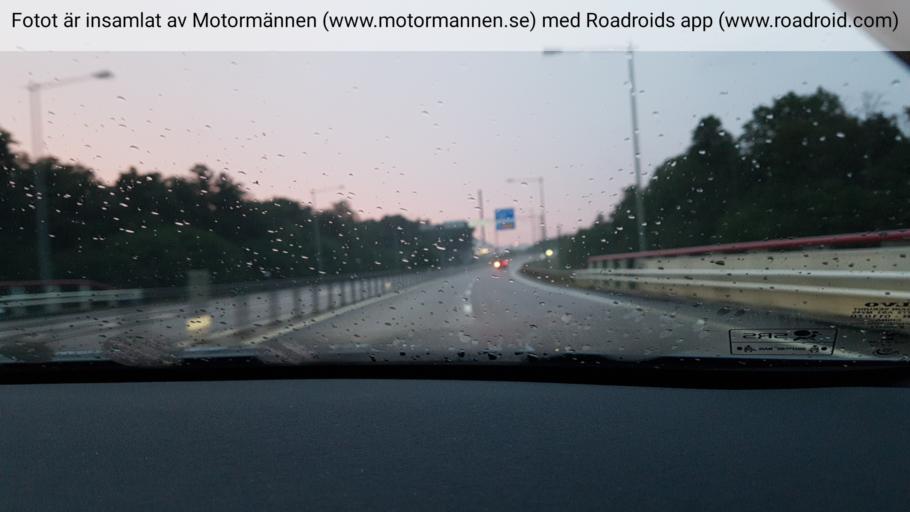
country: SE
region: Vaestra Goetaland
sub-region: Skovde Kommun
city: Skoevde
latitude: 58.3697
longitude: 13.8547
